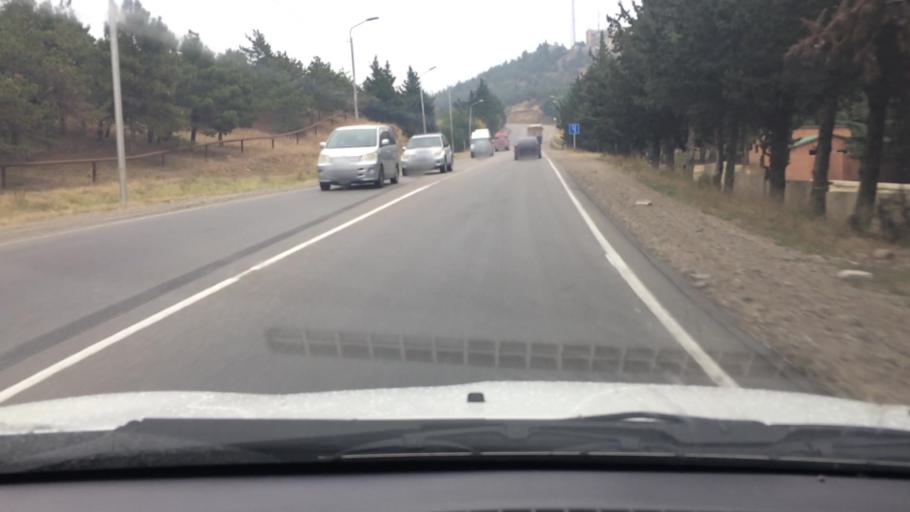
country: GE
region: T'bilisi
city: Tbilisi
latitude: 41.6208
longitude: 44.7964
